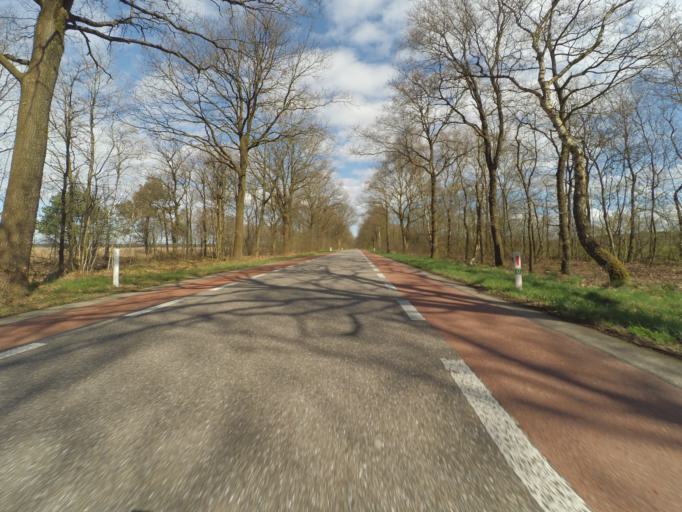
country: NL
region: Gelderland
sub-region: Gemeente Arnhem
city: Hoogkamp
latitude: 52.0911
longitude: 5.8790
